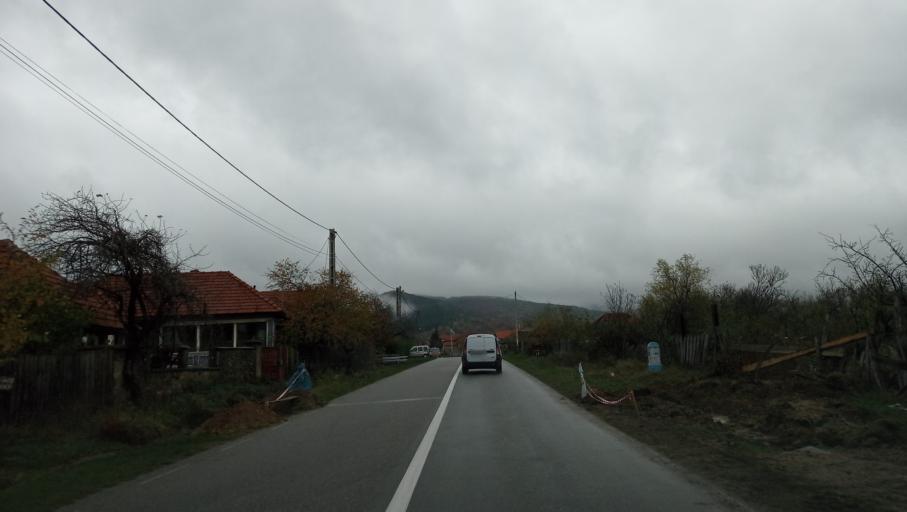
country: RO
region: Gorj
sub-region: Comuna Crasna
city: Crasna
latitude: 45.1689
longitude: 23.4838
